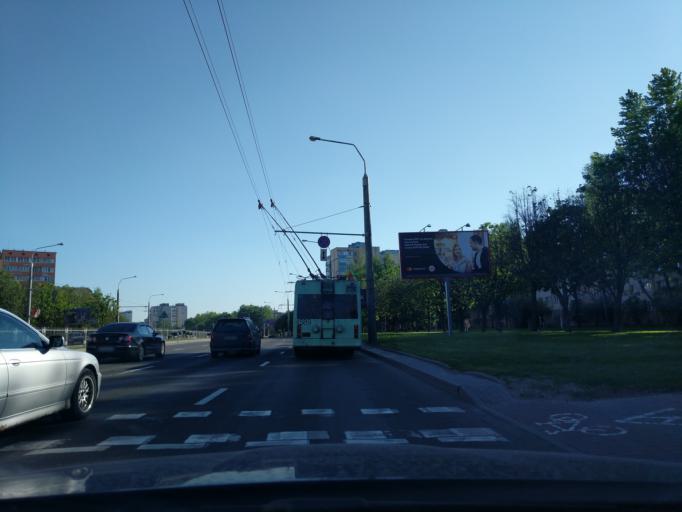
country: BY
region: Minsk
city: Novoye Medvezhino
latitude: 53.9181
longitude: 27.4958
